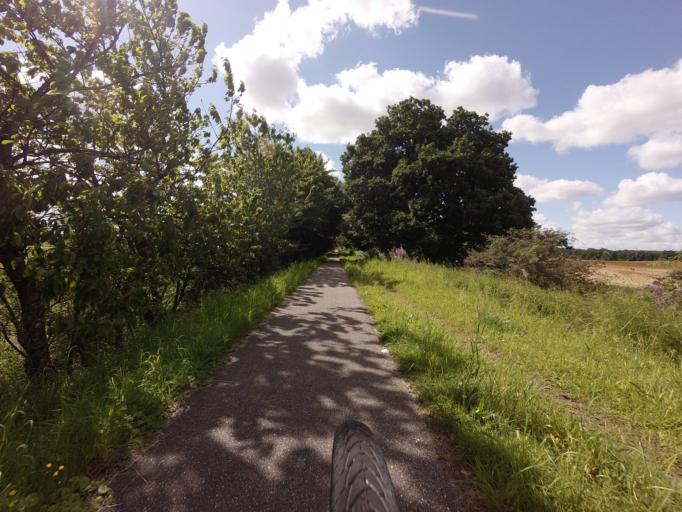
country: DK
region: Central Jutland
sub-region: Horsens Kommune
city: Horsens
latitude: 55.9231
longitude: 9.7681
